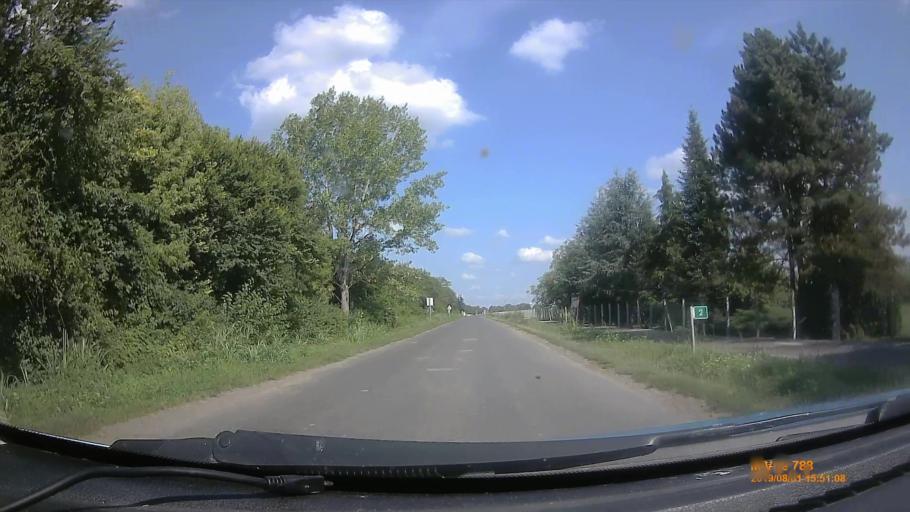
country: HU
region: Baranya
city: Szentlorinc
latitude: 46.0353
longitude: 18.0075
